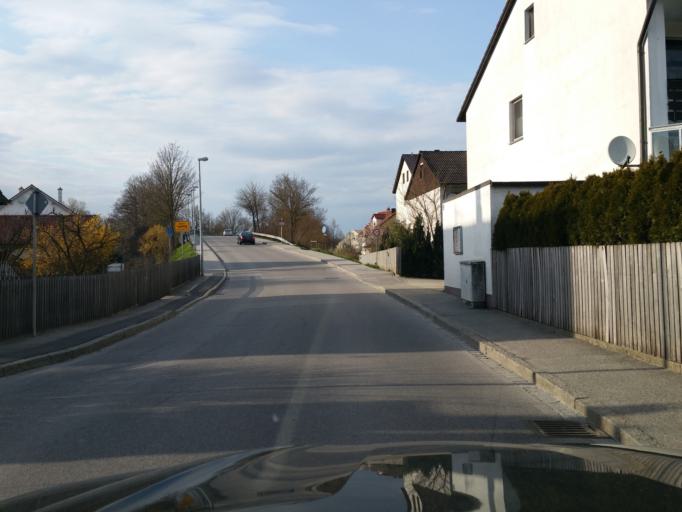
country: DE
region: Bavaria
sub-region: Lower Bavaria
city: Ergolding
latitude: 48.5584
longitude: 12.1689
